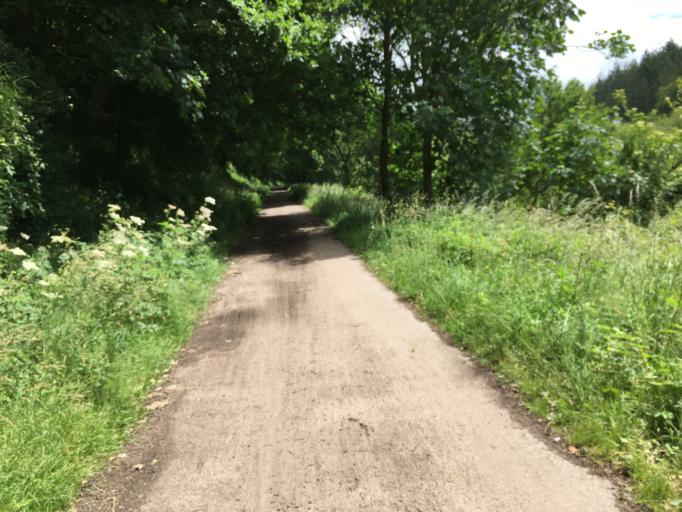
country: GB
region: England
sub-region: Cornwall
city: Wadebridge
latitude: 50.4993
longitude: -4.8086
